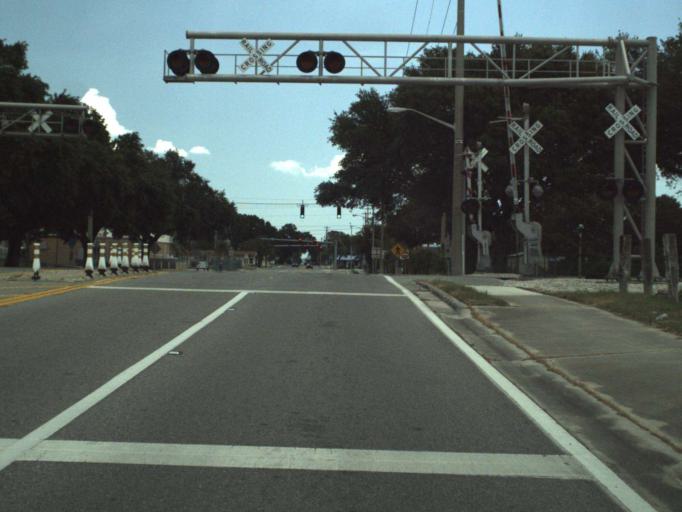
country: US
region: Florida
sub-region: Brevard County
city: Titusville
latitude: 28.6079
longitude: -80.8106
